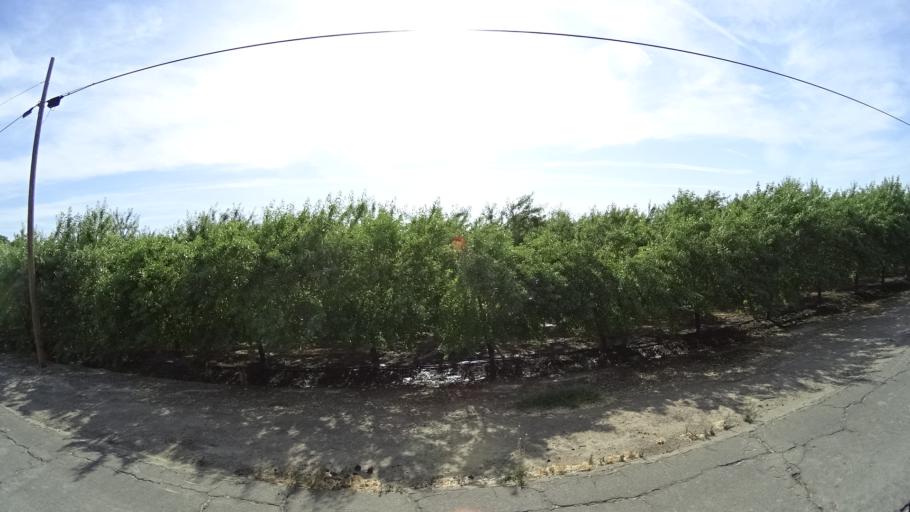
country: US
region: California
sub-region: Tulare County
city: Goshen
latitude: 36.3383
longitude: -119.4842
